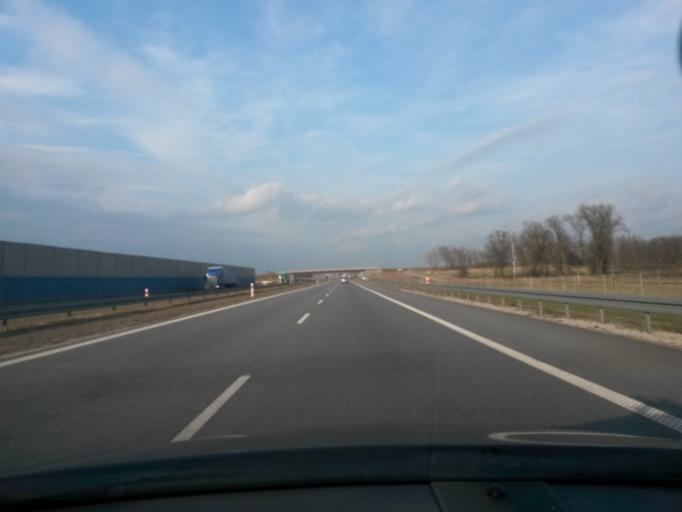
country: PL
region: Lodz Voivodeship
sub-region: Powiat brzezinski
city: Dmosin
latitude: 51.9338
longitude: 19.8053
